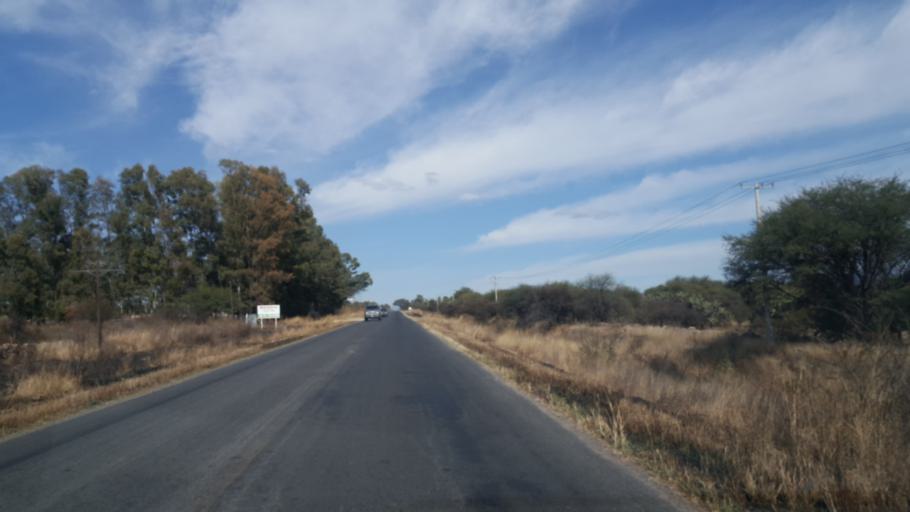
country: MX
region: Jalisco
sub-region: Lagos de Moreno
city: Cristeros [Fraccionamiento]
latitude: 21.2757
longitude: -101.9393
